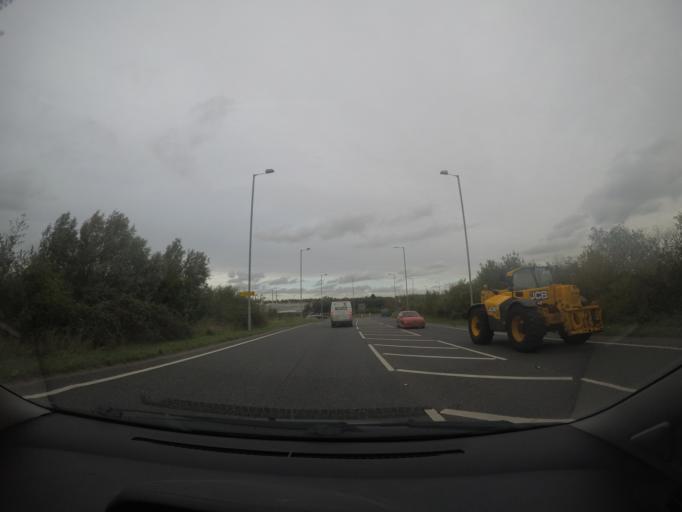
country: GB
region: England
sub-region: North Yorkshire
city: Barlby
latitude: 53.7894
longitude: -1.0397
